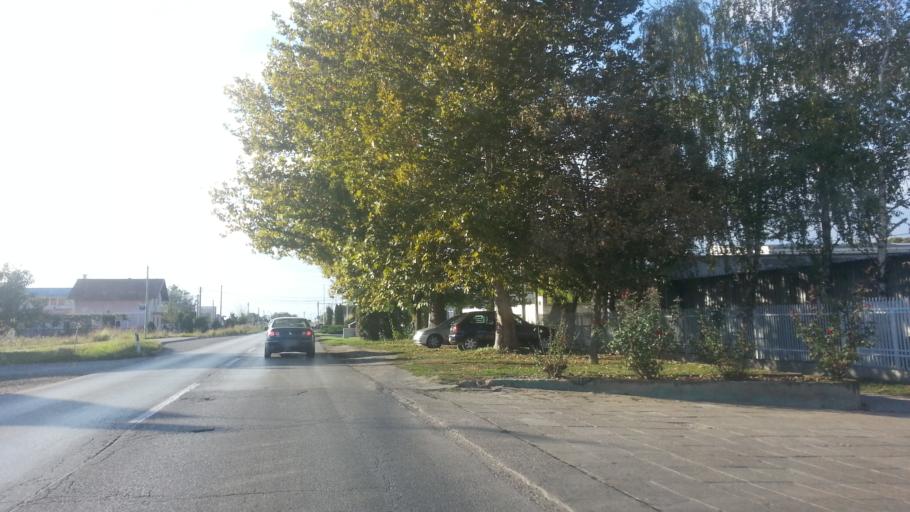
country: RS
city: Novi Banovci
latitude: 44.9138
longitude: 20.2606
